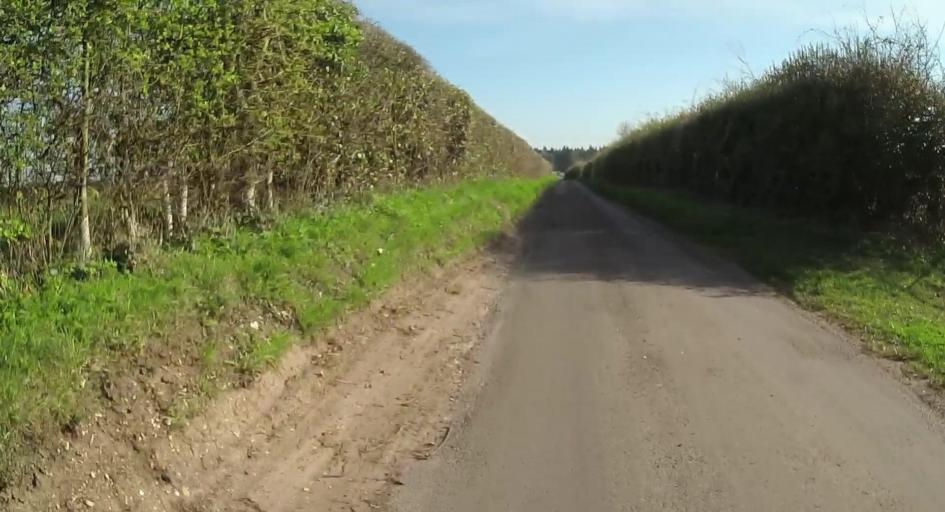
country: GB
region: England
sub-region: Hampshire
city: Highclere
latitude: 51.2604
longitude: -1.3687
